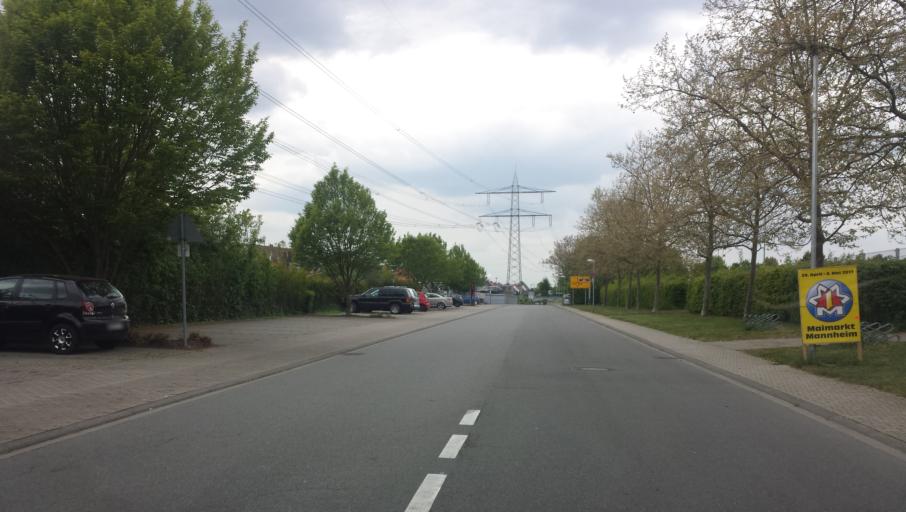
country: DE
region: Baden-Wuerttemberg
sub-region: Karlsruhe Region
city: Ketsch
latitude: 49.3706
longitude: 8.5402
